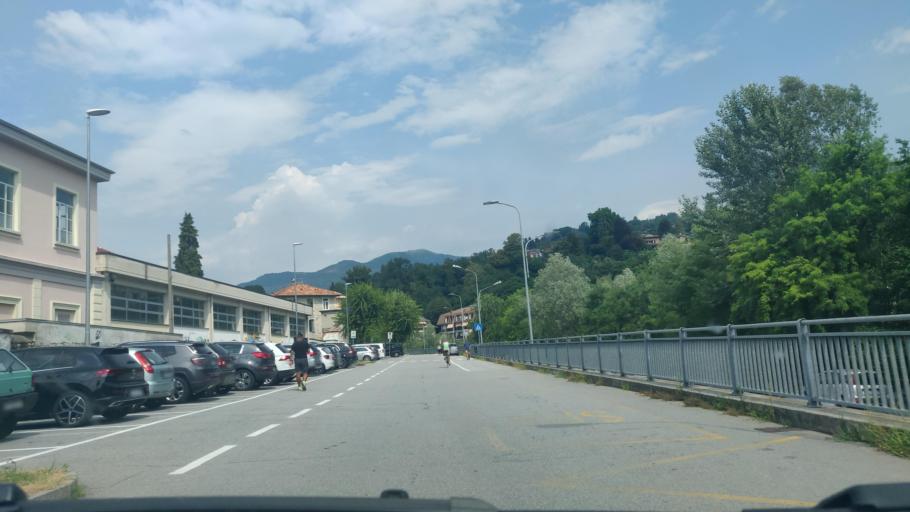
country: IT
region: Piedmont
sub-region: Provincia Verbano-Cusio-Ossola
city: Pallanza-Intra-Suna
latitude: 45.9402
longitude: 8.5767
